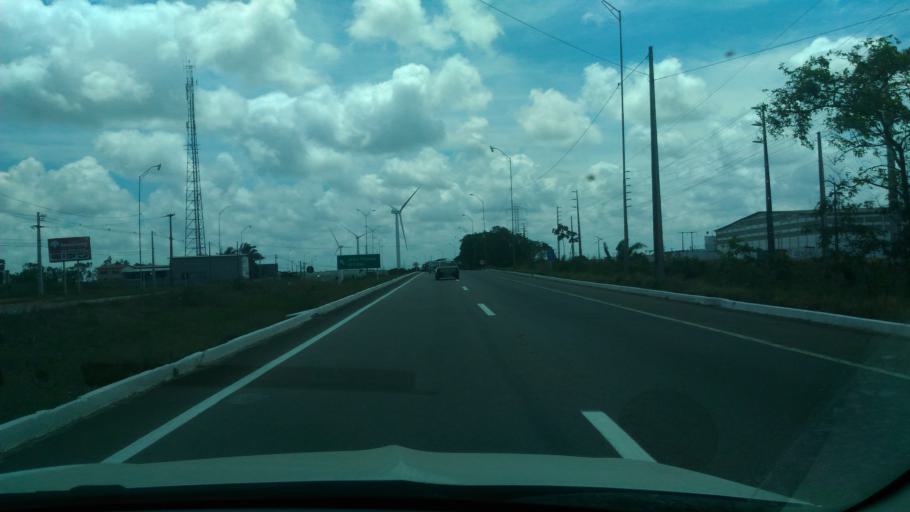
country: BR
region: Paraiba
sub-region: Conde
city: Conde
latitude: -7.2556
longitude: -34.9346
